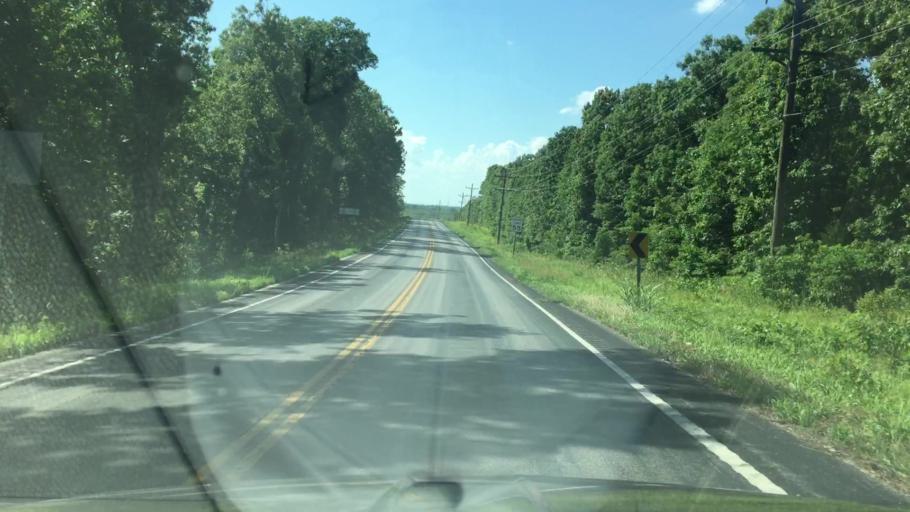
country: US
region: Missouri
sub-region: Camden County
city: Osage Beach
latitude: 38.1311
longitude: -92.5581
